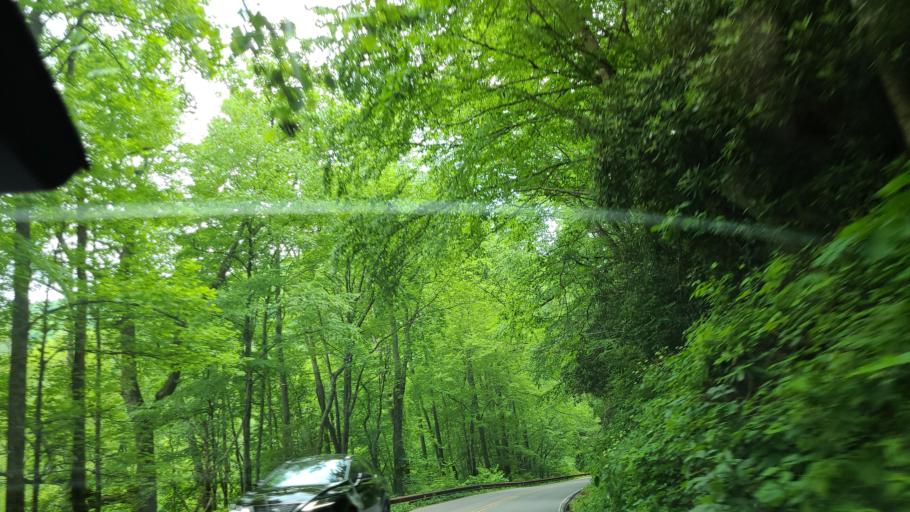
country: US
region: North Carolina
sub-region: Macon County
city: Franklin
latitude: 35.0847
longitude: -83.2658
